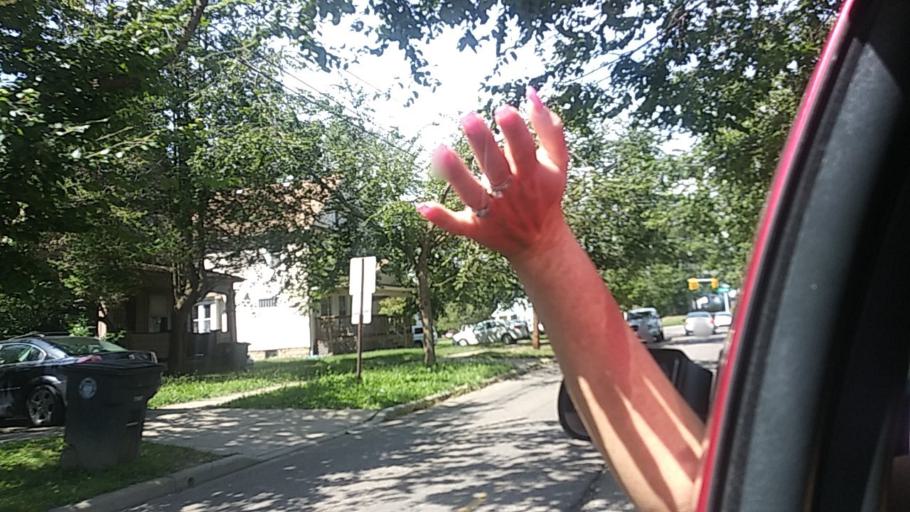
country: US
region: Ohio
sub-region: Summit County
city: Akron
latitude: 41.0834
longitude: -81.5495
